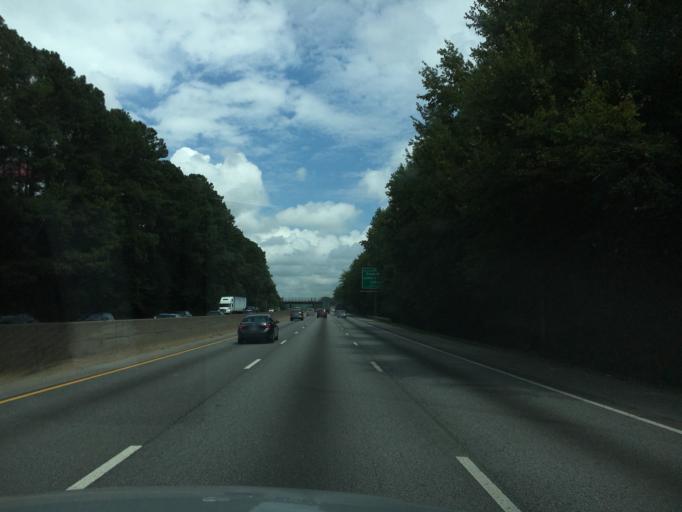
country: US
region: Georgia
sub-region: DeKalb County
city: Pine Mountain
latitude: 33.7032
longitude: -84.1512
